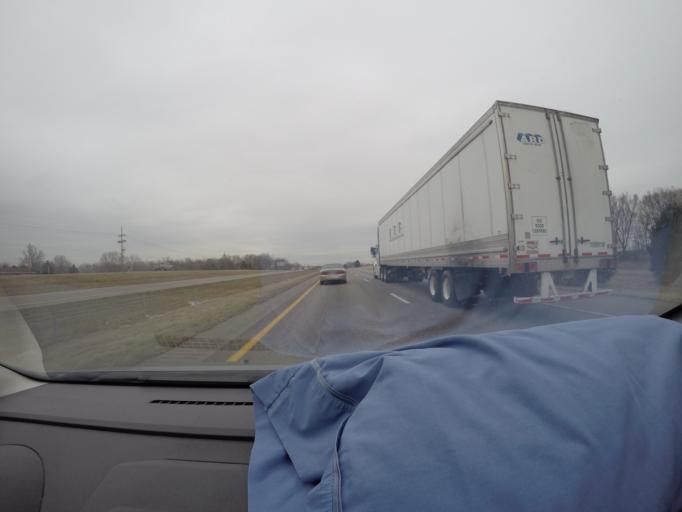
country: US
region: Missouri
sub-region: Saint Charles County
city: Wentzville
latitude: 38.8055
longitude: -90.9091
